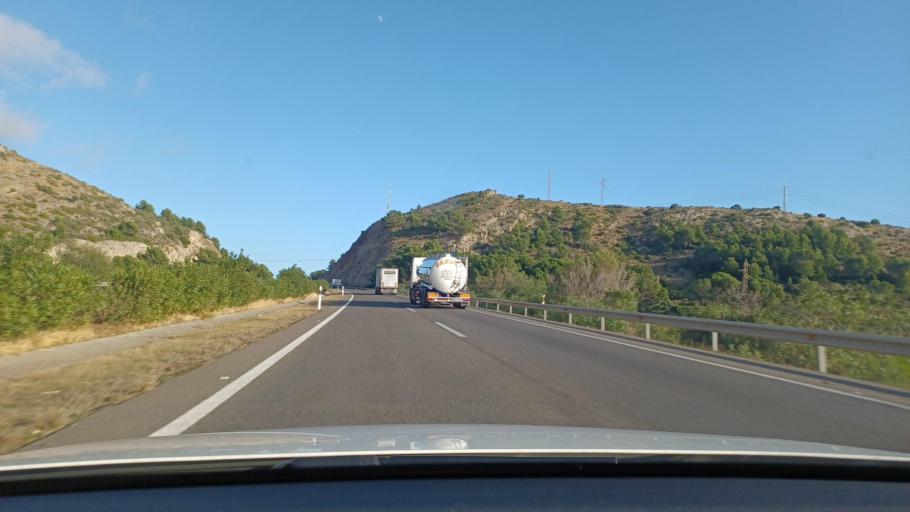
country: ES
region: Valencia
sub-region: Provincia de Castello
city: Benicassim
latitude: 40.0661
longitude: 0.0842
